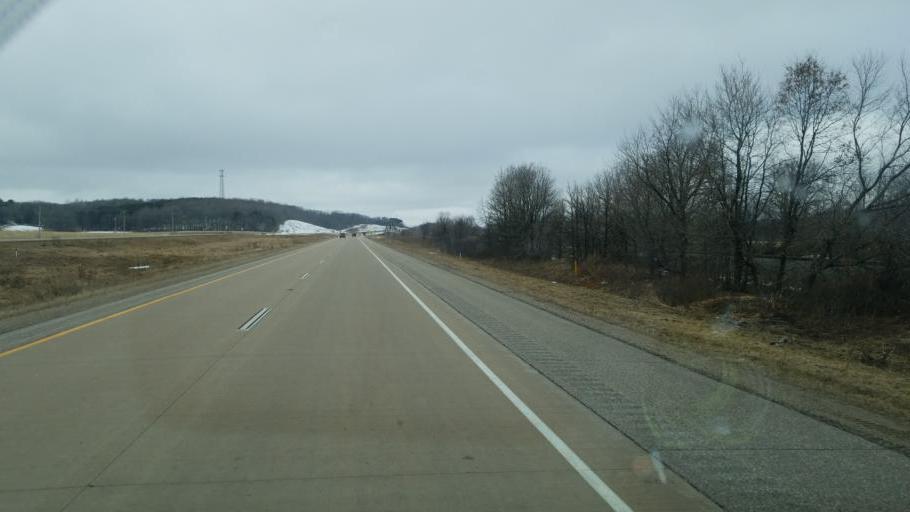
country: US
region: Wisconsin
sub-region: Portage County
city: Amherst
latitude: 44.4062
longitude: -89.2283
